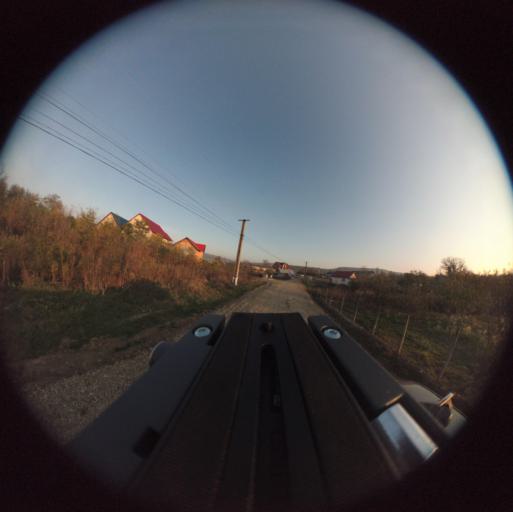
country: RO
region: Vaslui
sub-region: Comuna Bacesti
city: Bacesti
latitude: 46.8282
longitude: 27.2500
